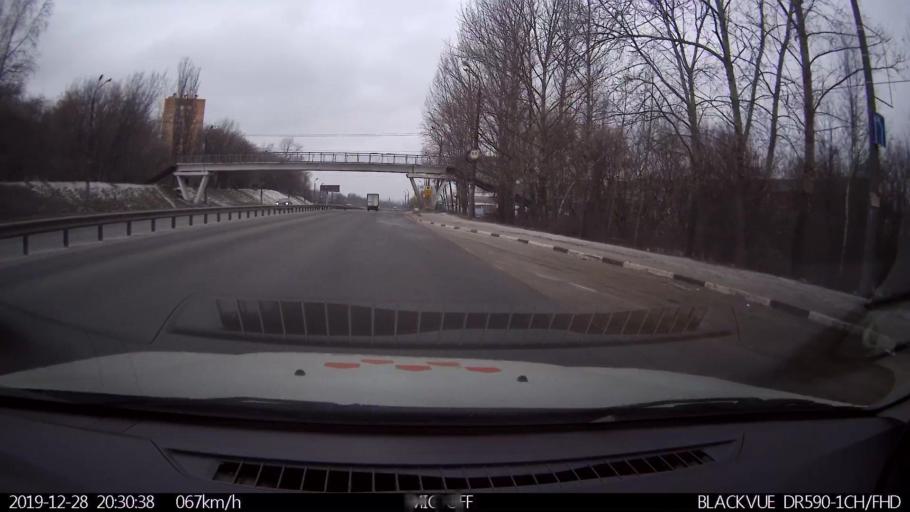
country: RU
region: Nizjnij Novgorod
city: Nizhniy Novgorod
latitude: 56.2392
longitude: 43.9692
